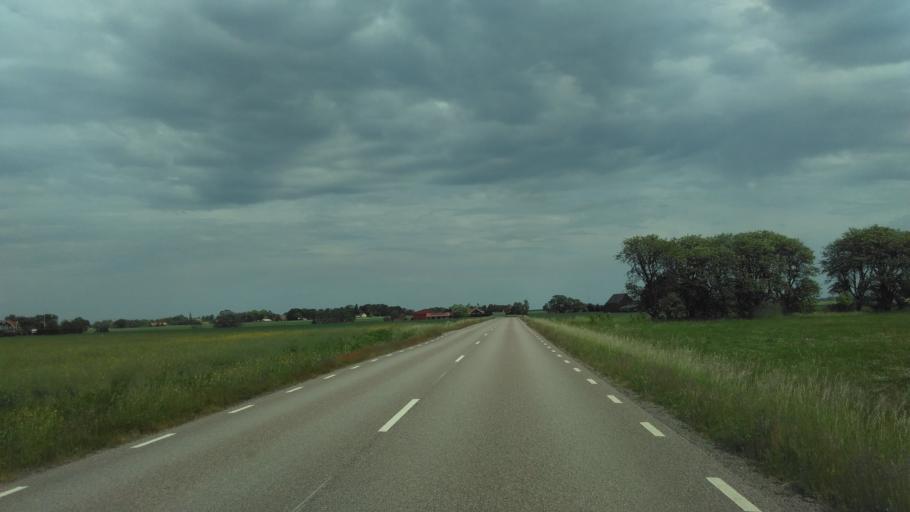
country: SE
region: Vaestra Goetaland
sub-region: Vara Kommun
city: Kvanum
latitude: 58.3595
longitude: 13.1395
